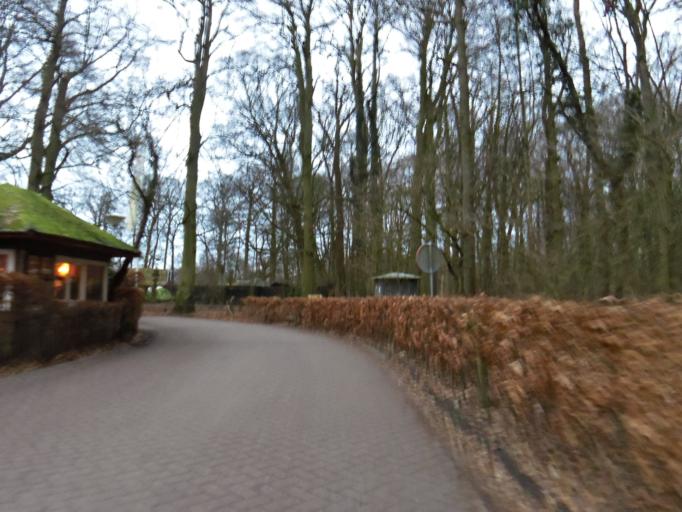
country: NL
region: North Holland
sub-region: Gemeente Bloemendaal
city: Bennebroek
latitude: 52.3307
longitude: 4.5659
